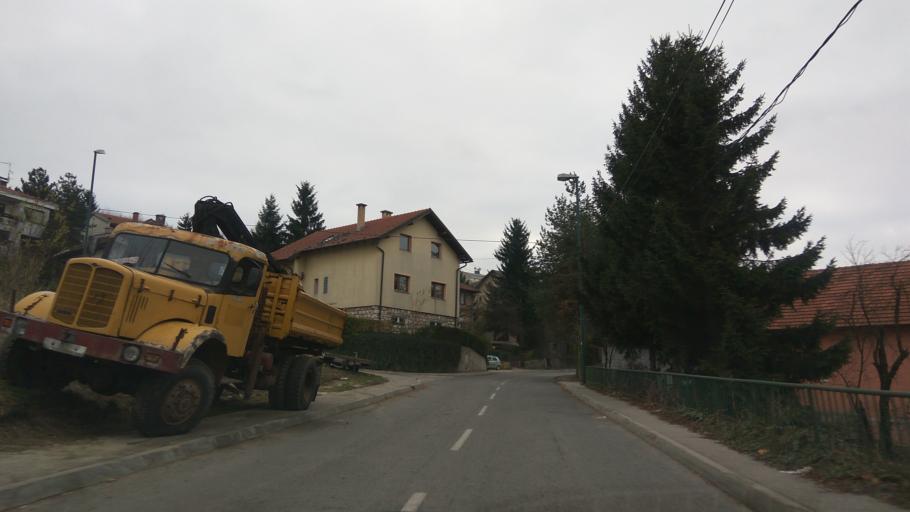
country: BA
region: Federation of Bosnia and Herzegovina
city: Kobilja Glava
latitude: 43.8625
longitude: 18.4035
